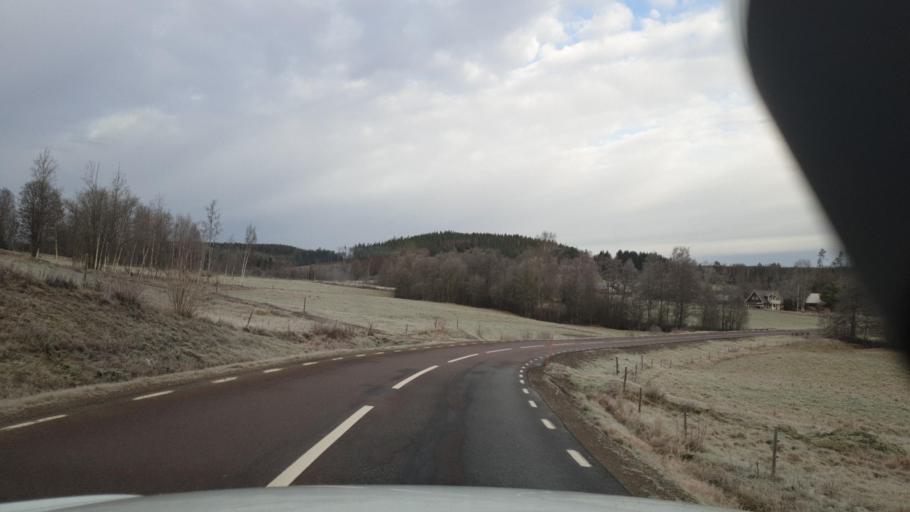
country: SE
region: Vaermland
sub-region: Sunne Kommun
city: Sunne
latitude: 59.6664
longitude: 13.0082
